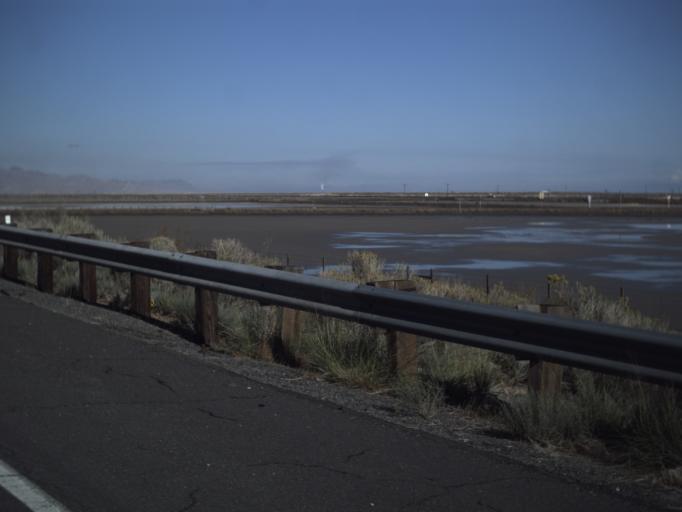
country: US
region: Utah
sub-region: Tooele County
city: Grantsville
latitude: 40.7085
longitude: -112.5259
